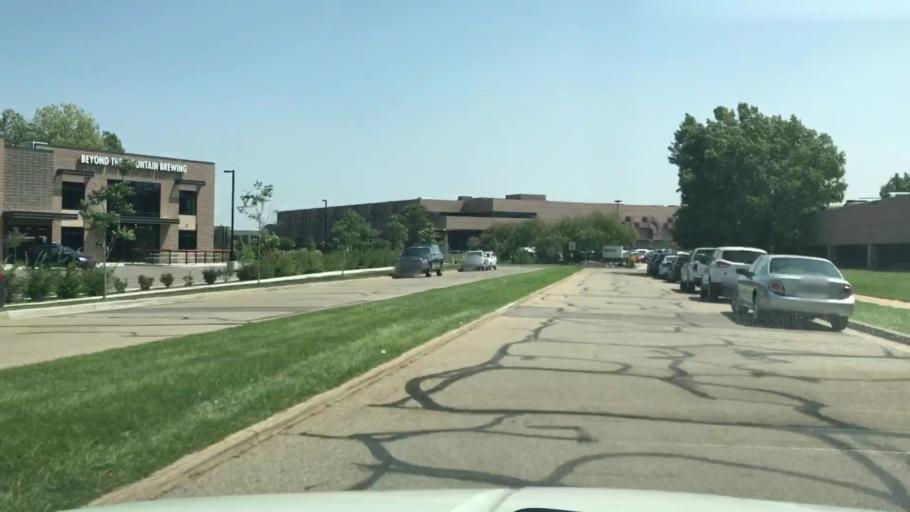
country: US
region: Colorado
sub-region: Boulder County
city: Gunbarrel
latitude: 40.0646
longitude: -105.2156
